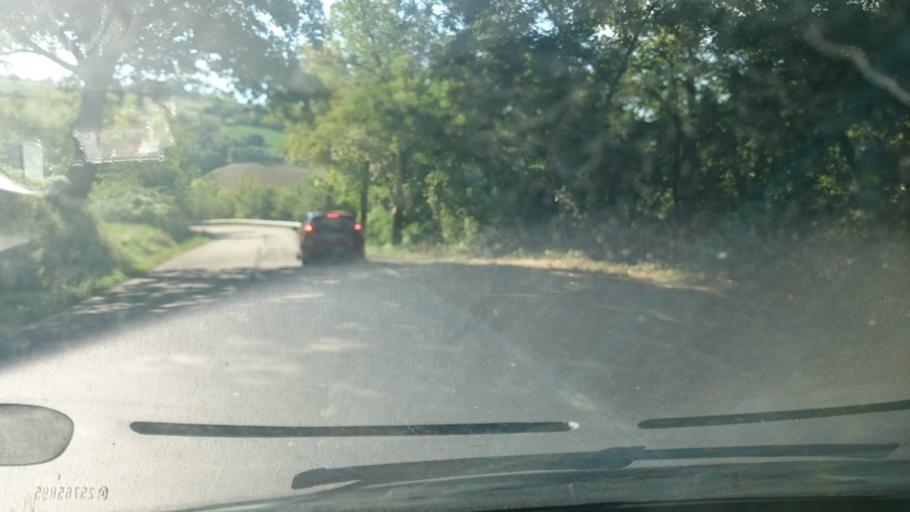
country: IT
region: Emilia-Romagna
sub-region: Provincia di Reggio Emilia
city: Villa Minozzo
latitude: 44.3712
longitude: 10.4606
